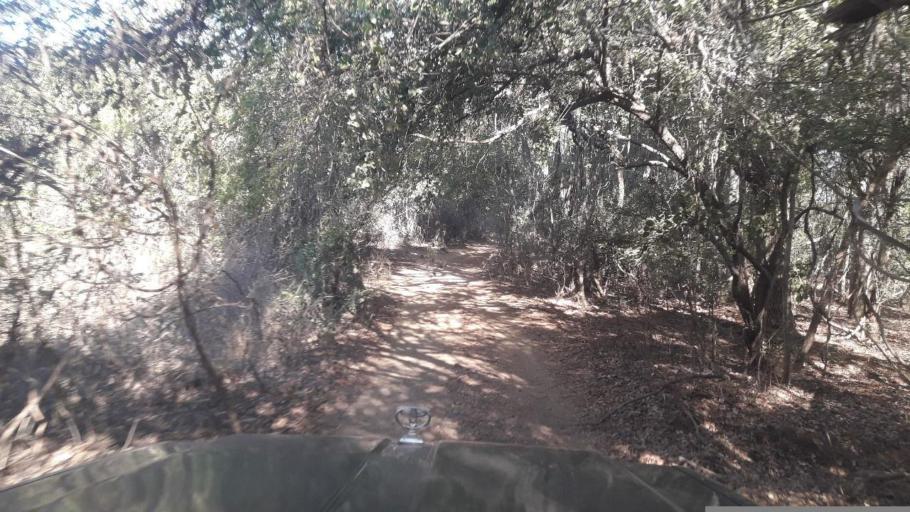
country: MG
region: Boeny
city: Sitampiky
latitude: -16.4105
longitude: 45.6020
